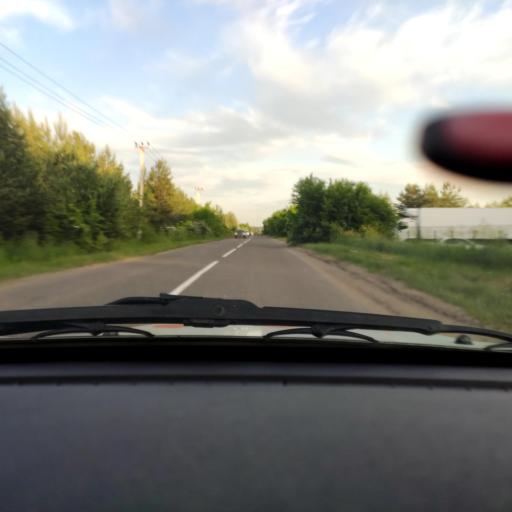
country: RU
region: Voronezj
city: Podgornoye
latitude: 51.8361
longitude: 39.2016
